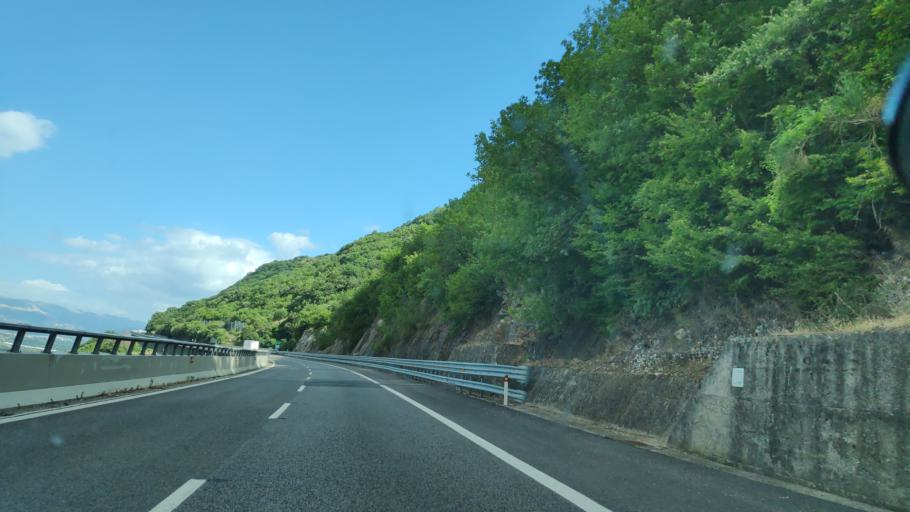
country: IT
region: Campania
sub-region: Provincia di Salerno
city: Sicignano degli Alburni
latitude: 40.5935
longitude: 15.3239
